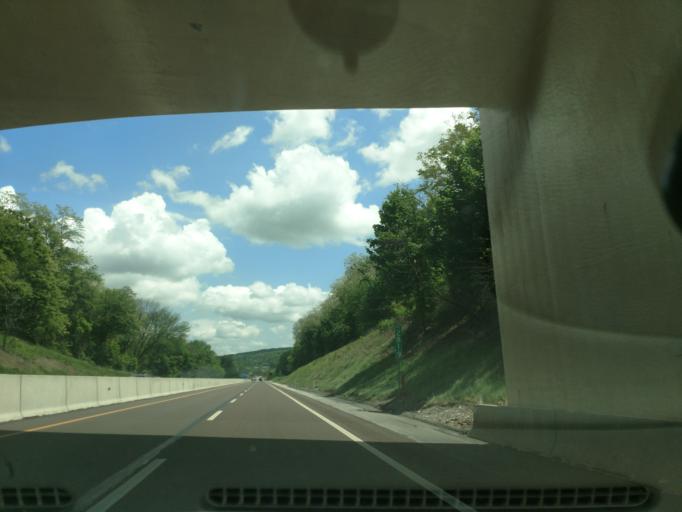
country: US
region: Pennsylvania
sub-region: Lancaster County
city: Denver
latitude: 40.2429
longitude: -76.1514
